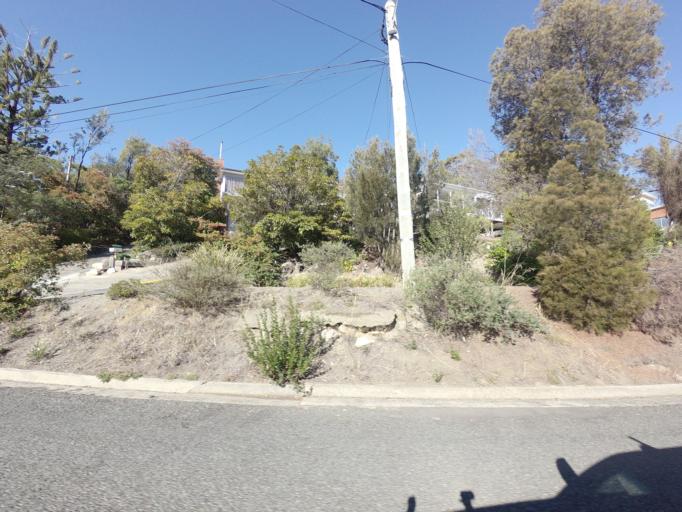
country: AU
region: Tasmania
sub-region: Clarence
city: Lindisfarne
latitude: -42.8432
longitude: 147.3393
